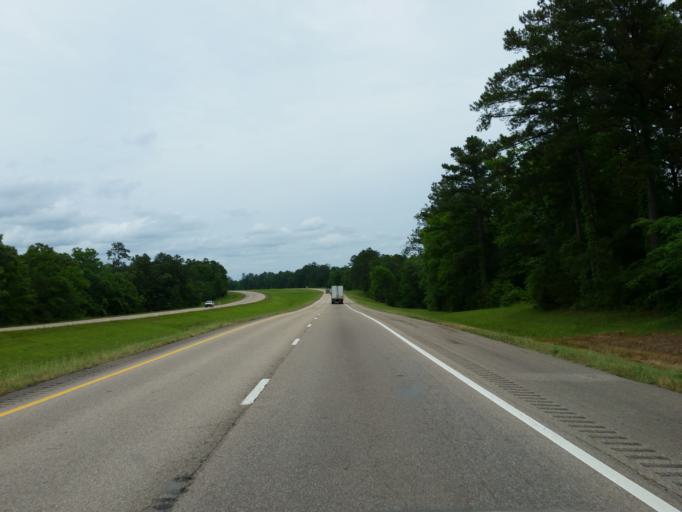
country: US
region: Mississippi
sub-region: Clarke County
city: Stonewall
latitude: 32.0103
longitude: -88.9289
